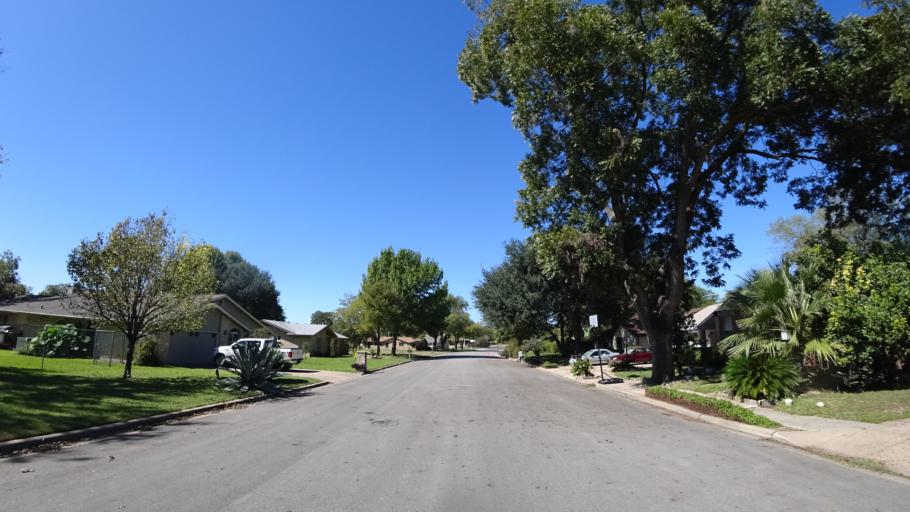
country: US
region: Texas
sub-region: Travis County
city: Hornsby Bend
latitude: 30.3047
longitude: -97.6551
